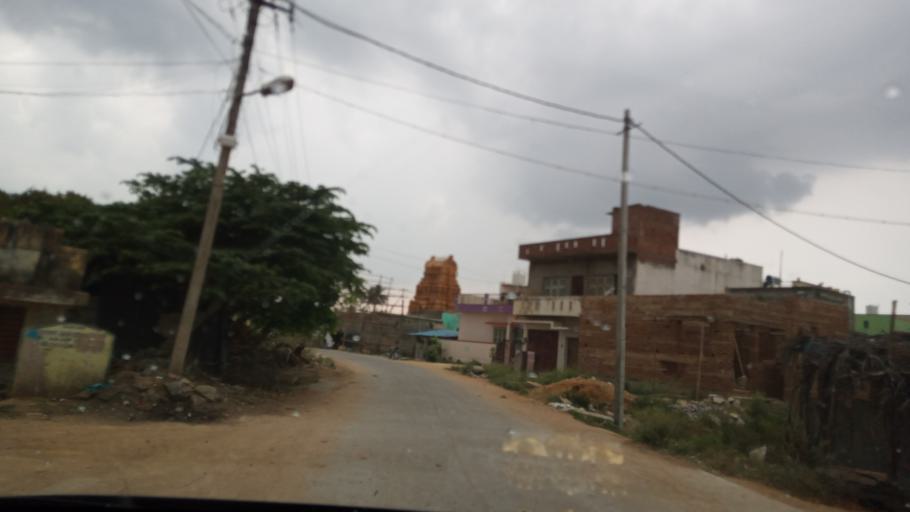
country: IN
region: Karnataka
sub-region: Kolar
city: Mulbagal
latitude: 13.1443
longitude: 78.3679
